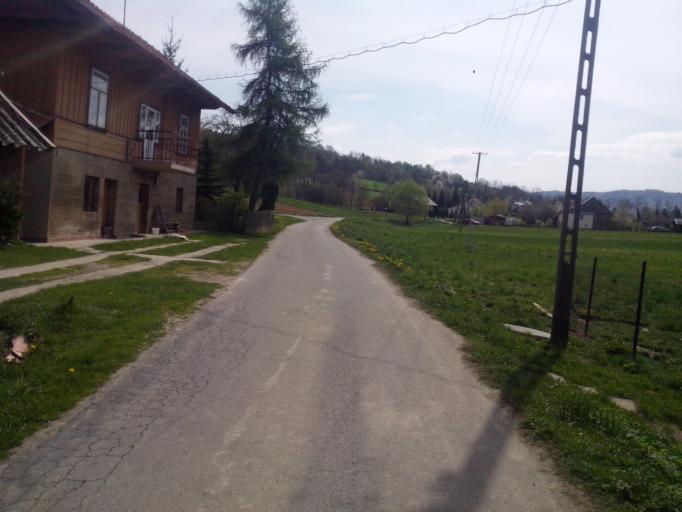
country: PL
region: Subcarpathian Voivodeship
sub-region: Powiat strzyzowski
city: Jawornik
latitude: 49.8220
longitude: 21.8404
